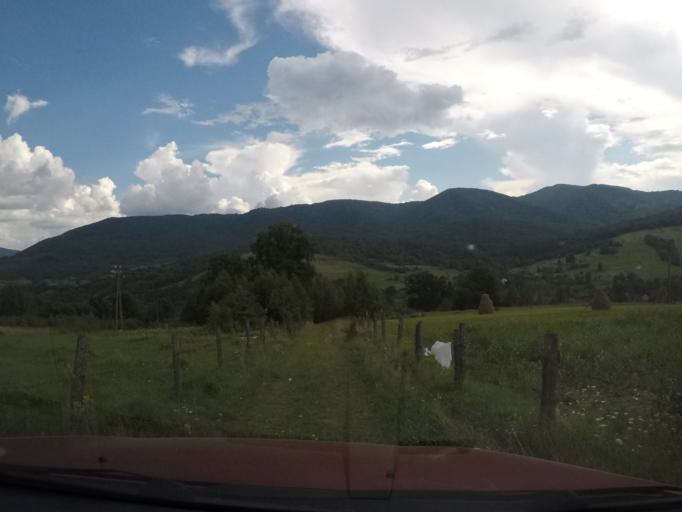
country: UA
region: Zakarpattia
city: Velykyi Bereznyi
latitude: 49.0322
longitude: 22.5922
